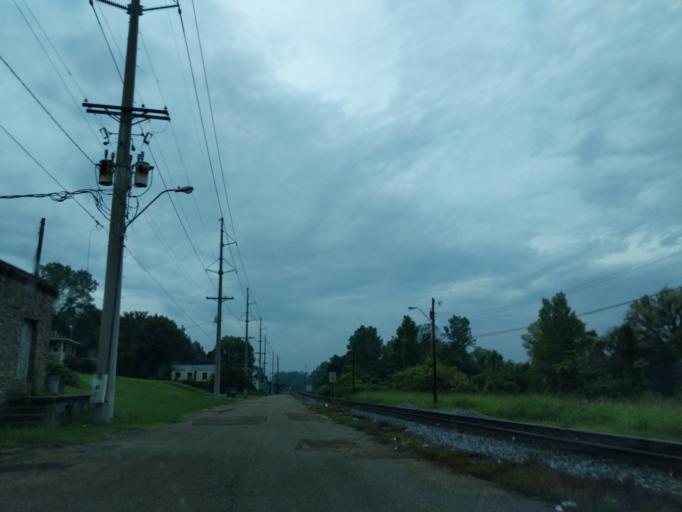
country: US
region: Mississippi
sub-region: Warren County
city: Vicksburg
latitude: 32.3397
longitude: -90.8881
